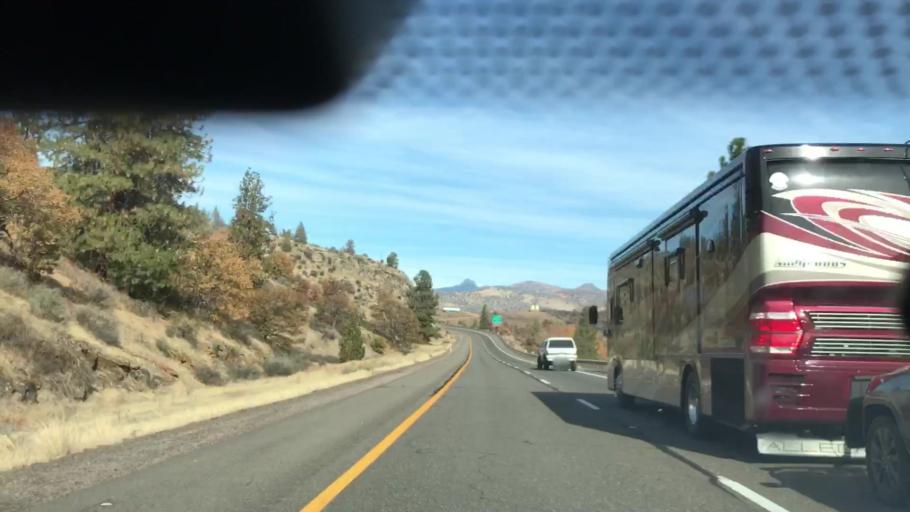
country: US
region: California
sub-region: Siskiyou County
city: Montague
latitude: 41.8814
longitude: -122.5558
